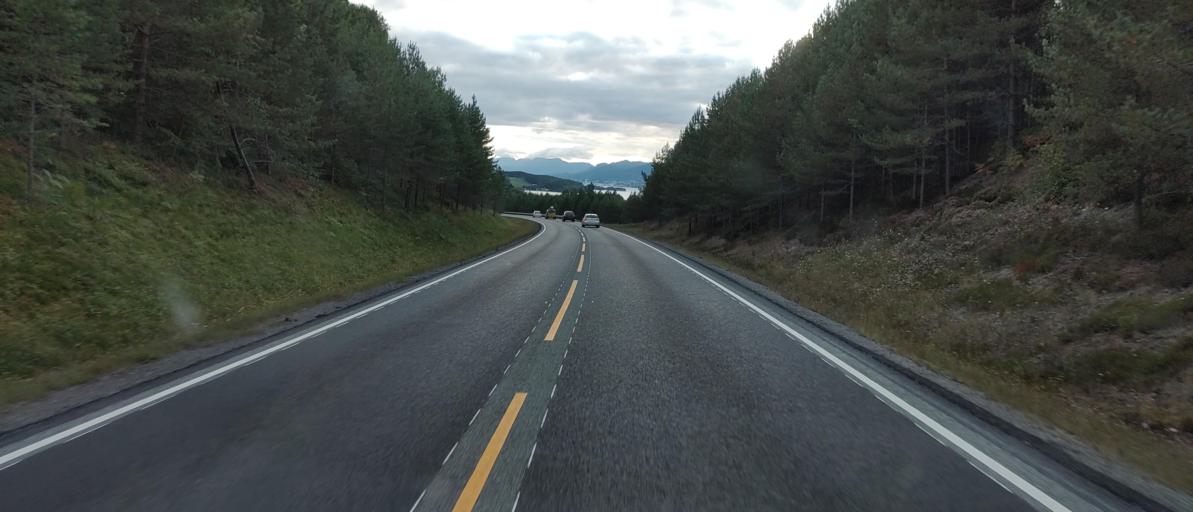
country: NO
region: More og Romsdal
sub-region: Molde
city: Hjelset
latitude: 62.7350
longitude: 7.3897
